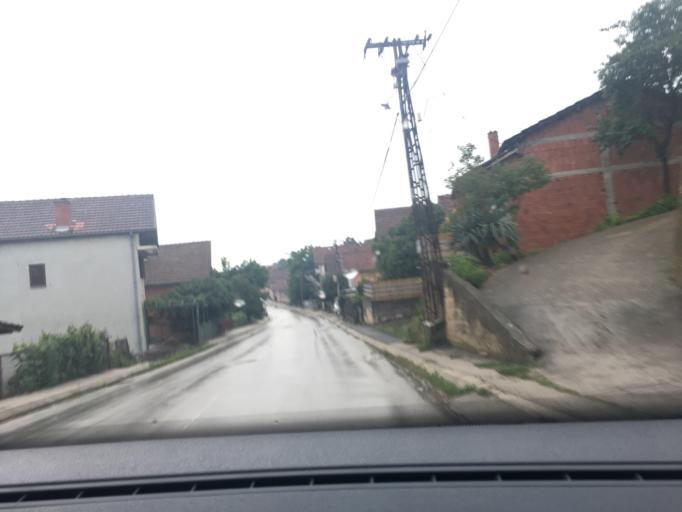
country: RS
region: Central Serbia
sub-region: Nisavski Okrug
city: Aleksinac
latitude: 43.5485
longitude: 21.7066
